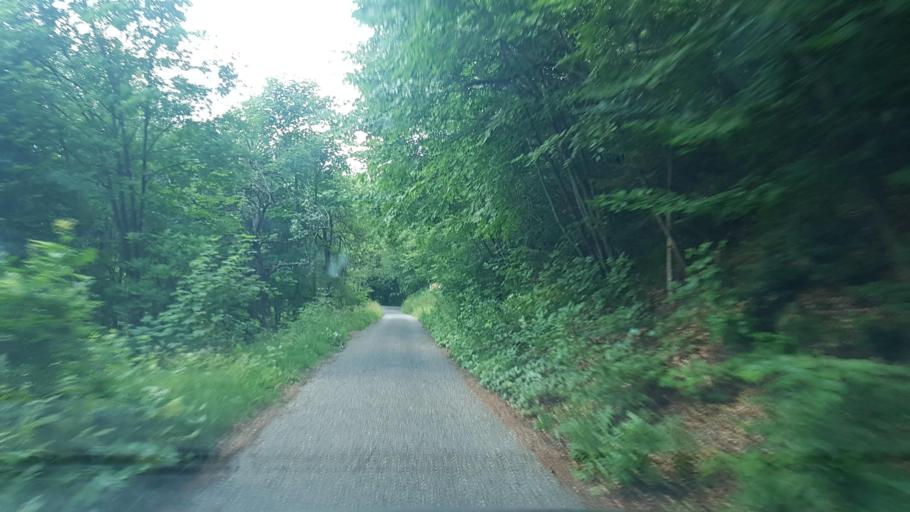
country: IT
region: Friuli Venezia Giulia
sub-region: Provincia di Udine
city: Paularo
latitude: 46.4755
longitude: 13.0958
